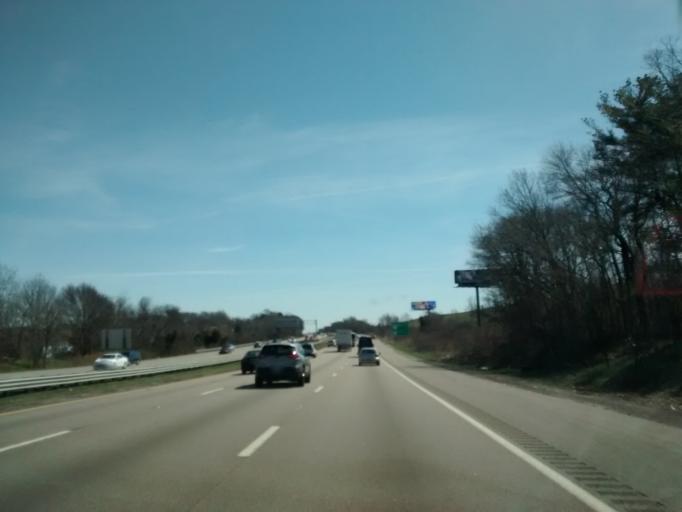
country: US
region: Massachusetts
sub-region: Norfolk County
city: Randolph
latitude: 42.1816
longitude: -71.0761
